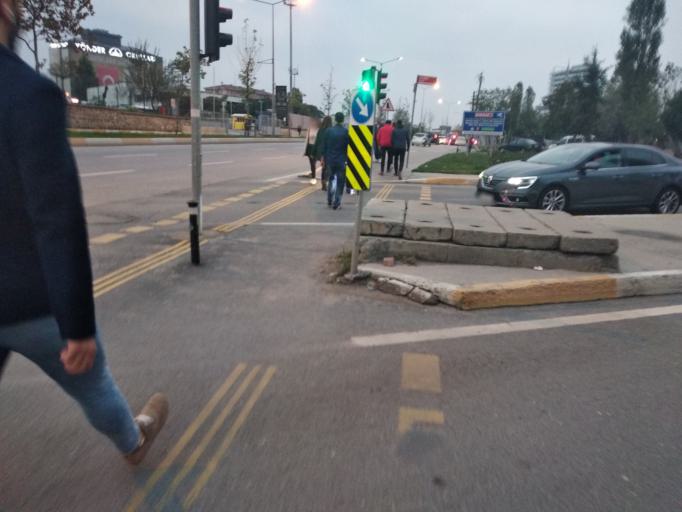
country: TR
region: Istanbul
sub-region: Atasehir
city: Atasehir
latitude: 40.9808
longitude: 29.1308
